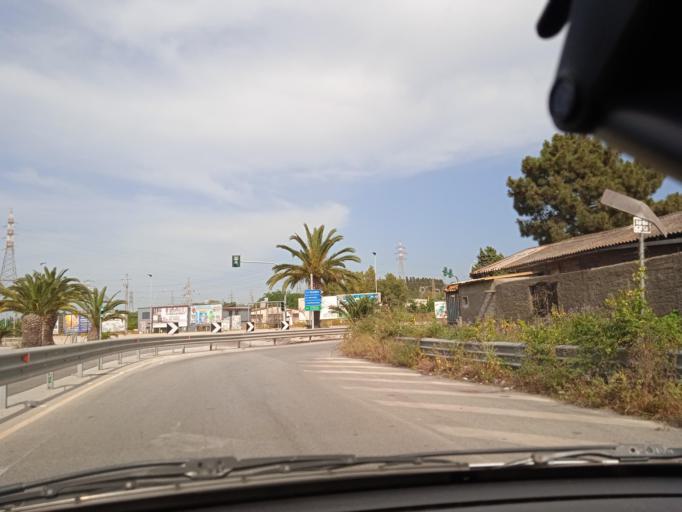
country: IT
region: Sicily
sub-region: Messina
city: San Filippo del Mela
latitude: 38.1852
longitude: 15.2697
